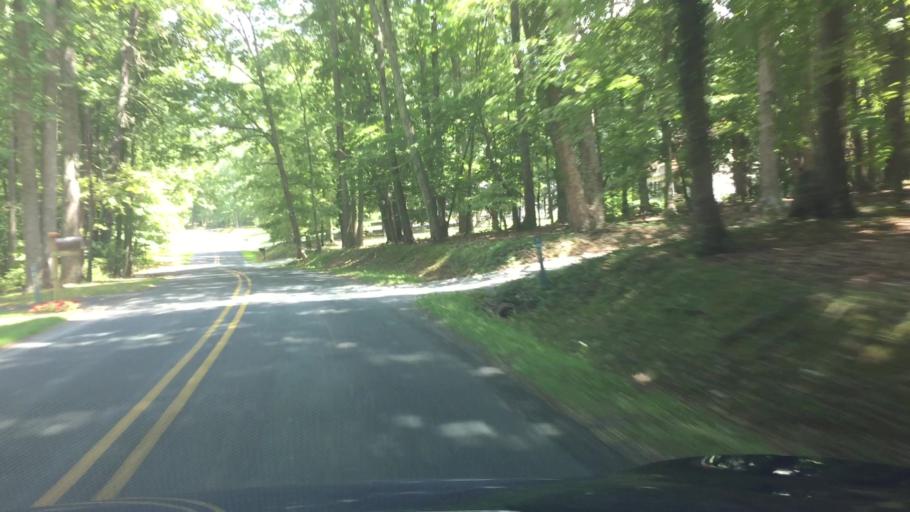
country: US
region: Virginia
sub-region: Appomattox County
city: Appomattox
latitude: 37.3302
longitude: -78.8772
